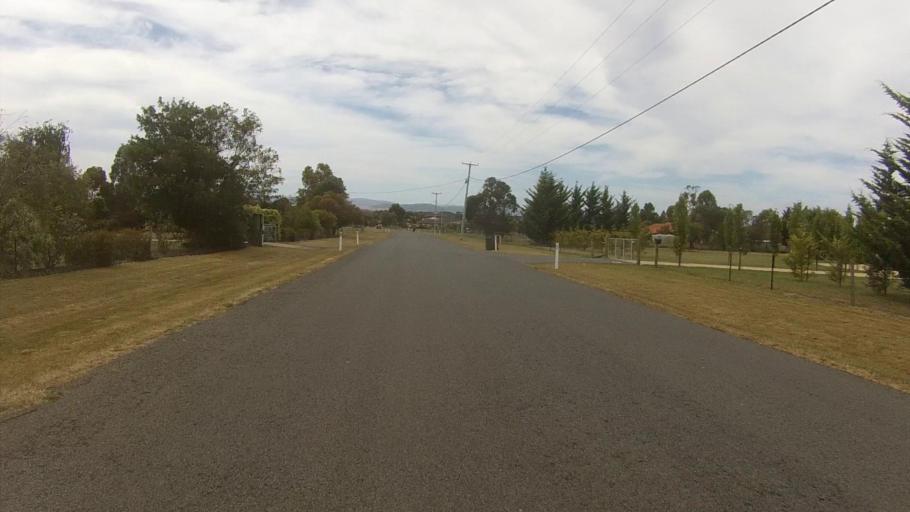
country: AU
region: Tasmania
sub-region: Clarence
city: Cambridge
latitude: -42.8472
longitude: 147.4702
